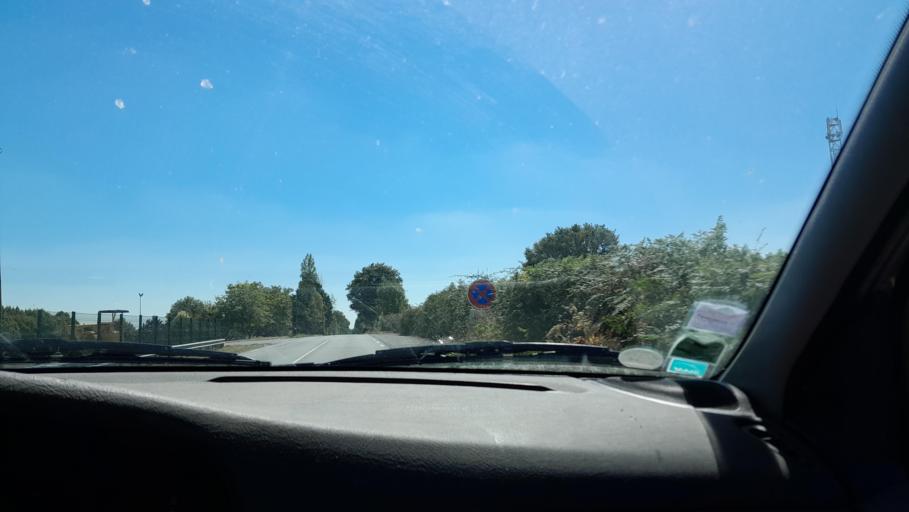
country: FR
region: Pays de la Loire
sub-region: Departement de Maine-et-Loire
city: Pouance
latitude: 47.6722
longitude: -1.1877
